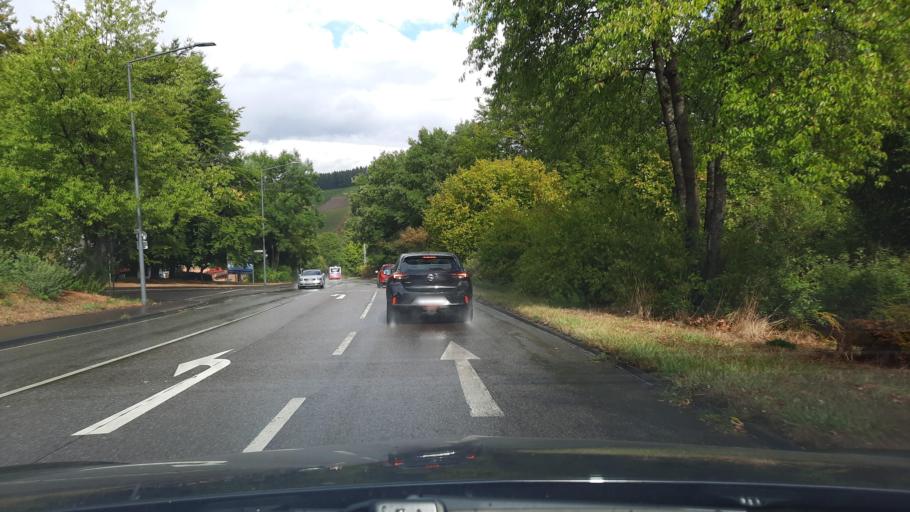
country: DE
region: Rheinland-Pfalz
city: Irsch
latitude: 49.7546
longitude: 6.6824
